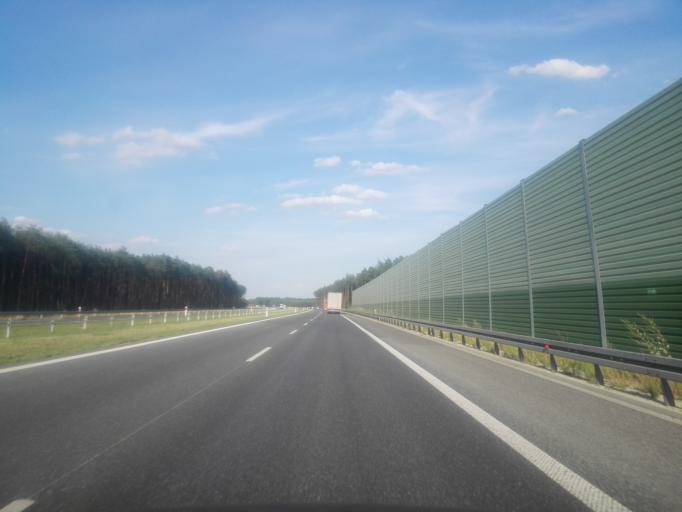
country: PL
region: Greater Poland Voivodeship
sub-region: Powiat kepinski
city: Perzow
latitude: 51.2963
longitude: 17.8427
